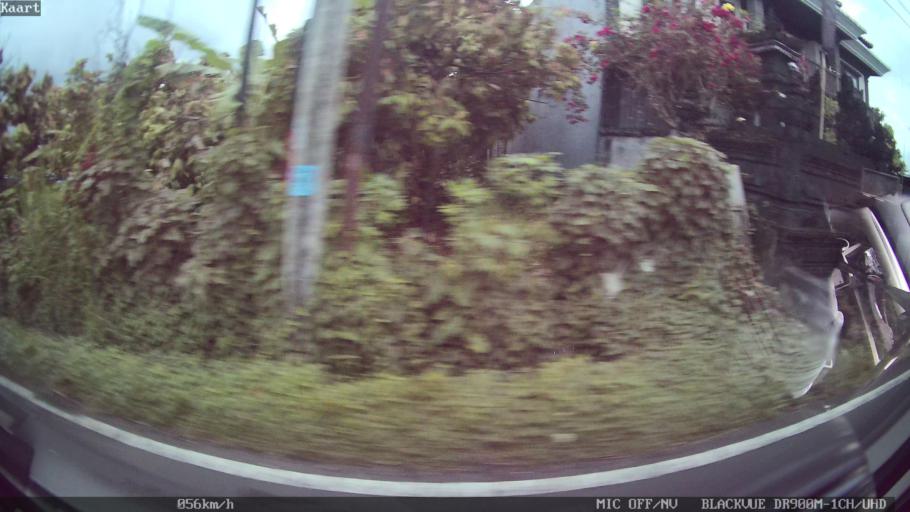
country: ID
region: Bali
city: Banjar Serangan
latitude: -8.5567
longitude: 115.1801
